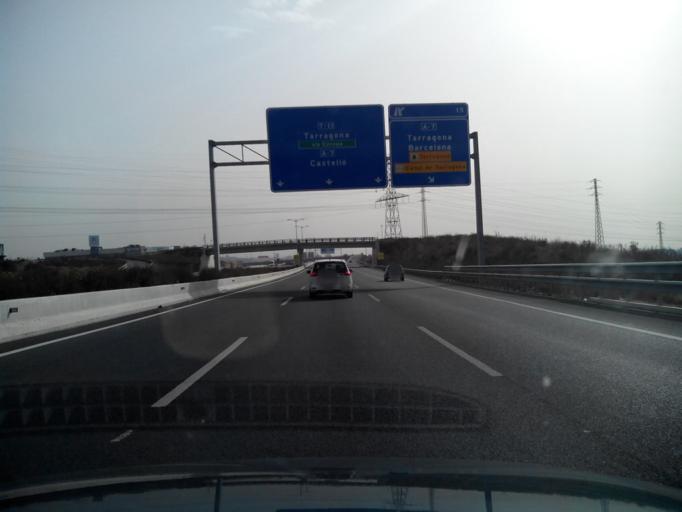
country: ES
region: Catalonia
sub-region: Provincia de Tarragona
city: Constanti
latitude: 41.1303
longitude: 1.1938
